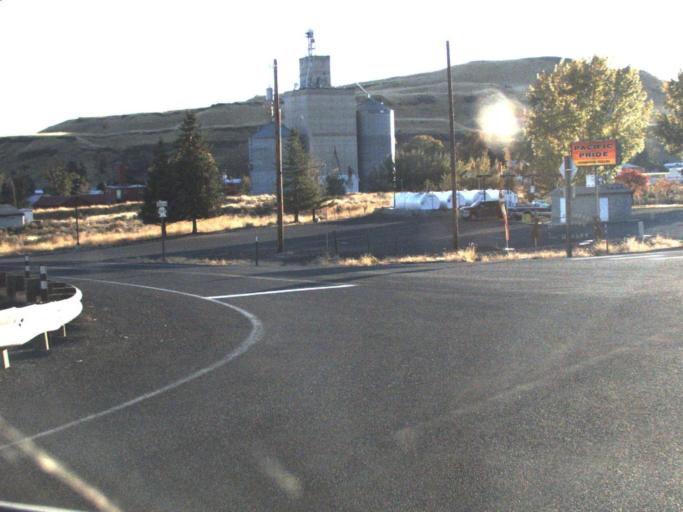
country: US
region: Washington
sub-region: Franklin County
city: Connell
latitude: 46.6447
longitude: -118.5528
